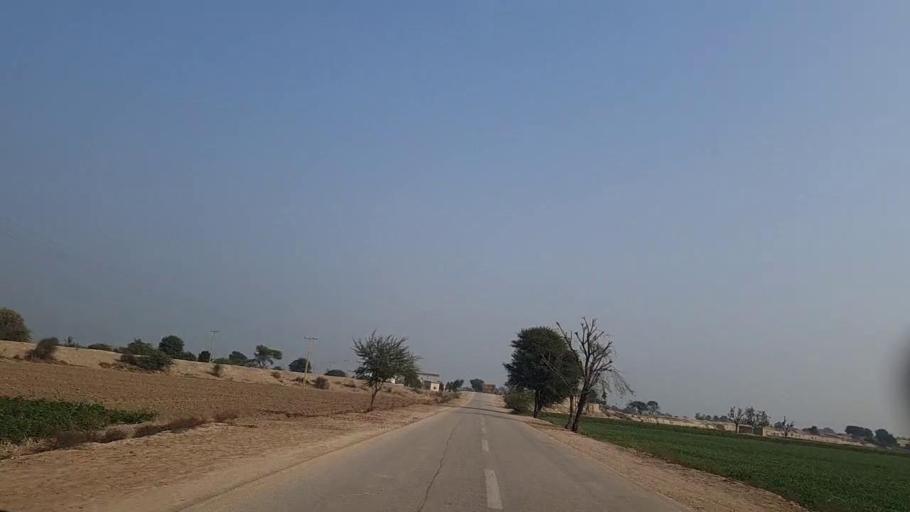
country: PK
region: Sindh
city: Sann
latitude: 26.1455
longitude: 68.1418
